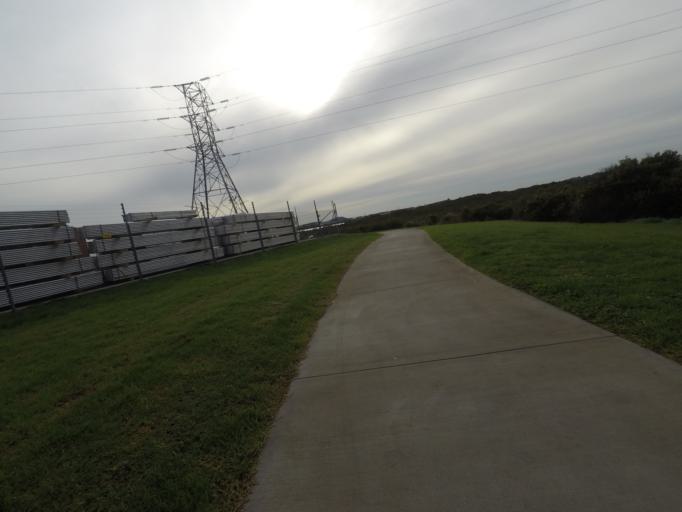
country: NZ
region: Auckland
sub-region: Auckland
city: Mangere
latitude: -36.9424
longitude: 174.7970
